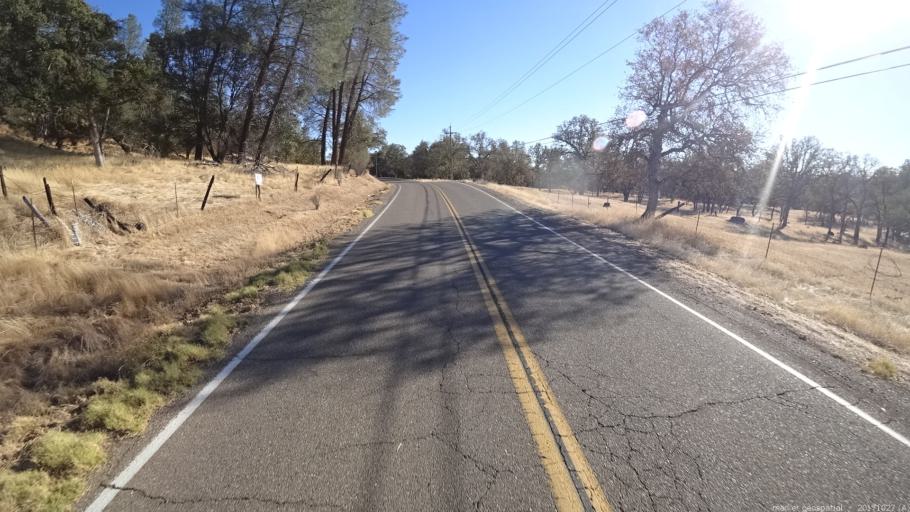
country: US
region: California
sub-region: Shasta County
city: Palo Cedro
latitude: 40.5601
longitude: -122.1887
